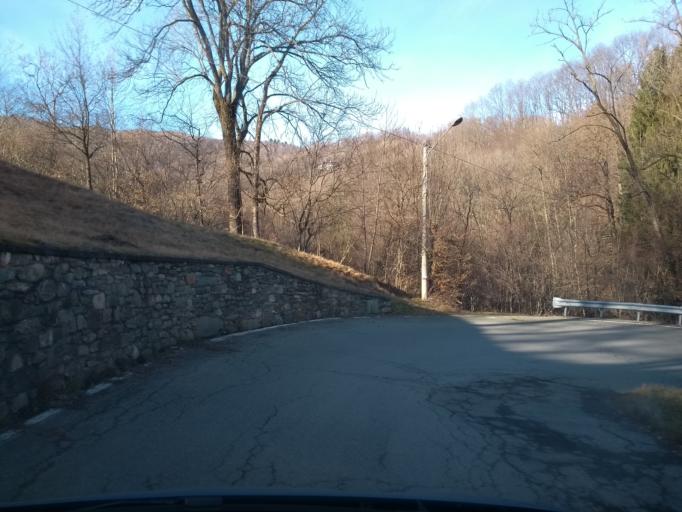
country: IT
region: Piedmont
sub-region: Provincia di Torino
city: Coassolo Torinese
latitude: 45.2808
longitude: 7.4639
